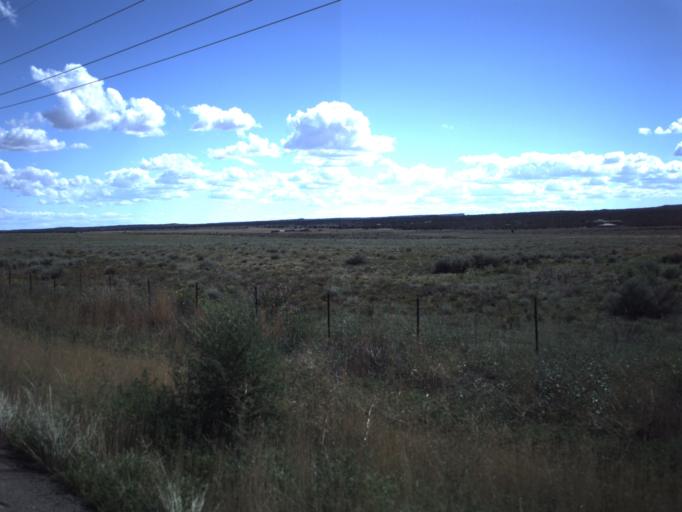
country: US
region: Arizona
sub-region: Mohave County
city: Colorado City
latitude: 37.0814
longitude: -113.1098
